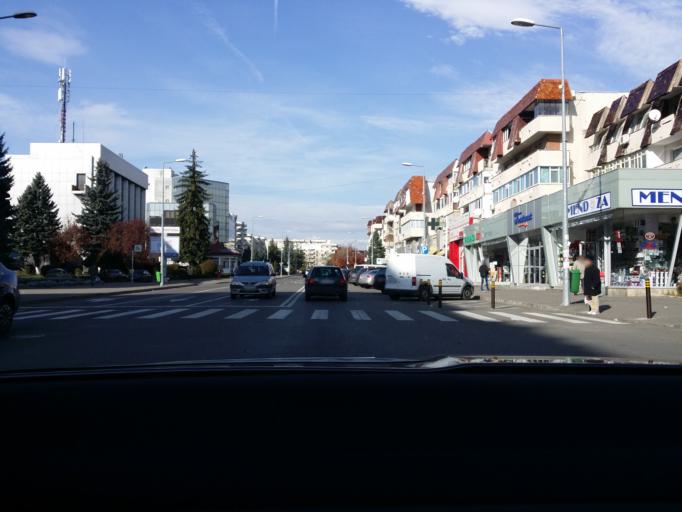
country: RO
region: Prahova
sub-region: Municipiul Campina
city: Campina
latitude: 45.1233
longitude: 25.7358
